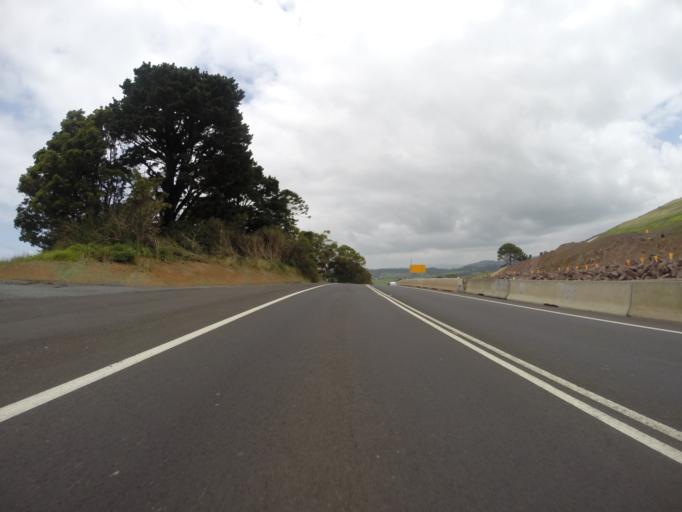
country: AU
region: New South Wales
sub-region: Kiama
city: Gerringong
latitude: -34.7466
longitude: 150.8050
